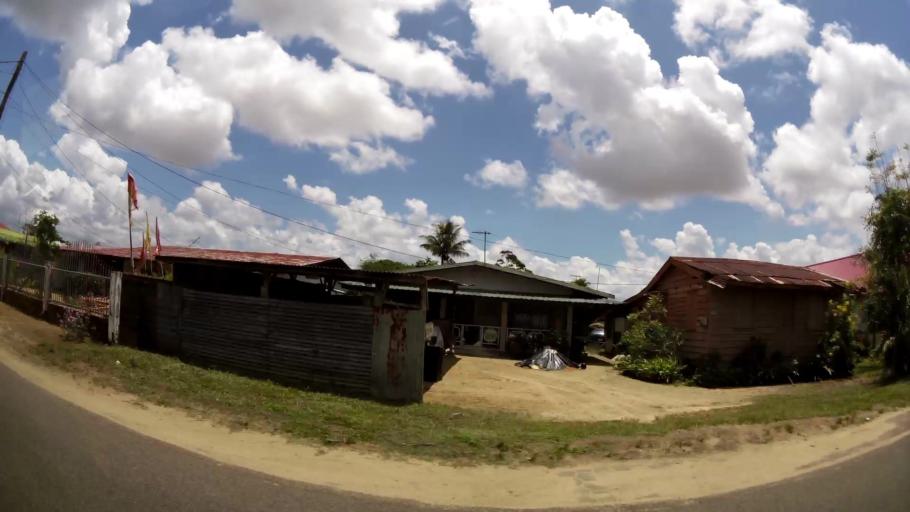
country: SR
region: Paramaribo
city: Paramaribo
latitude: 5.7976
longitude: -55.1321
